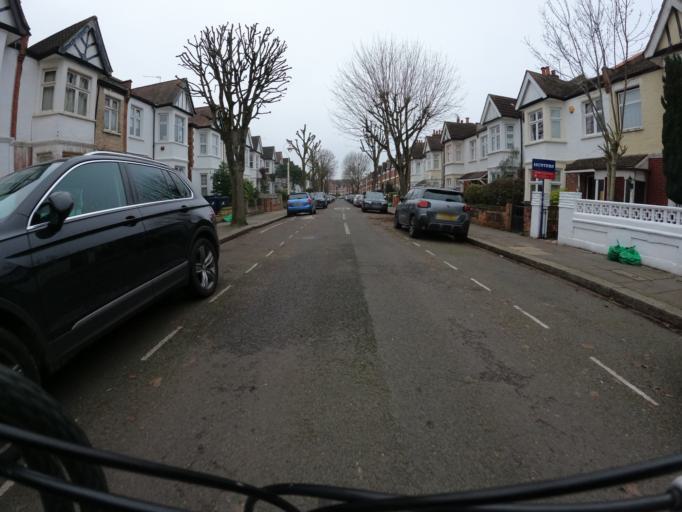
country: GB
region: England
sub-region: Greater London
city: Ealing
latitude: 51.5055
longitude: -0.3158
